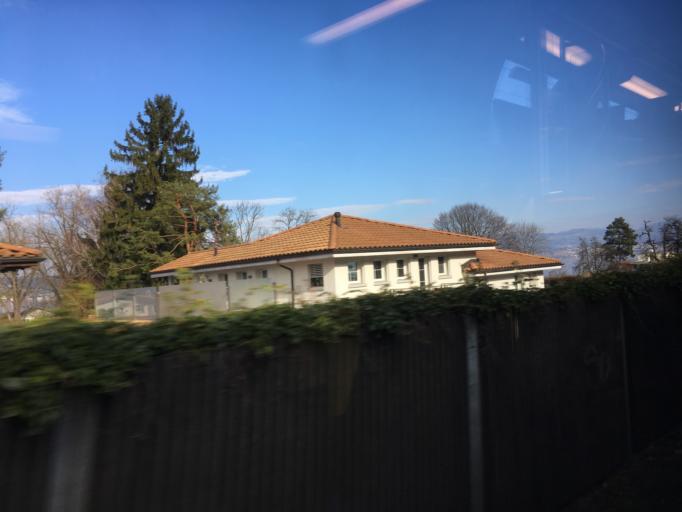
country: CH
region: Schwyz
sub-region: Bezirk Hoefe
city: Freienbach
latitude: 47.2058
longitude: 8.7438
